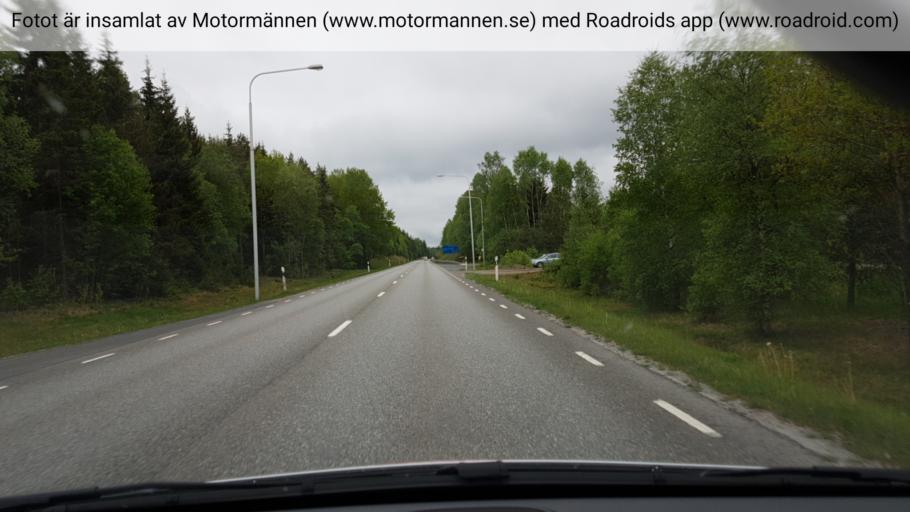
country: SE
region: Joenkoeping
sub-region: Gnosjo Kommun
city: Marieholm
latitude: 57.6020
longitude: 13.7476
